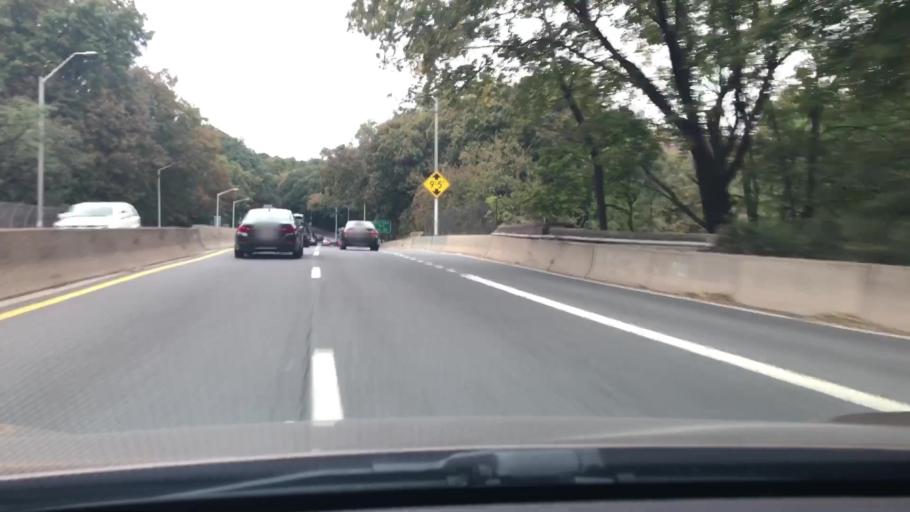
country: US
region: New York
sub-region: Westchester County
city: Yonkers
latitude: 40.9002
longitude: -73.8967
